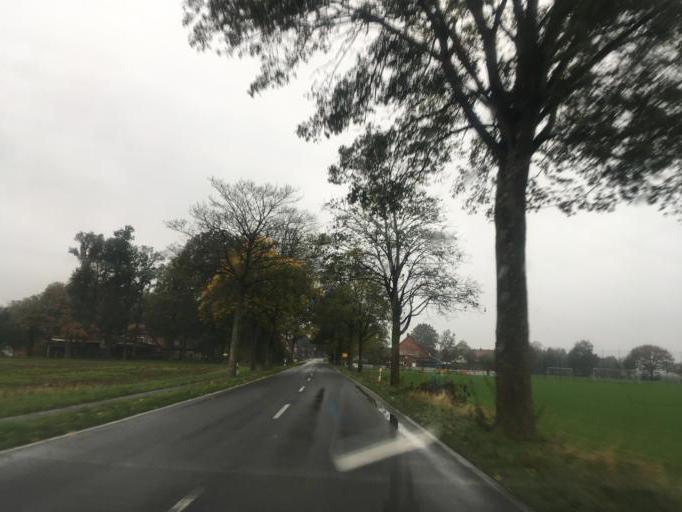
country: DE
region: Lower Saxony
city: Bergen
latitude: 52.8157
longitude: 10.0027
